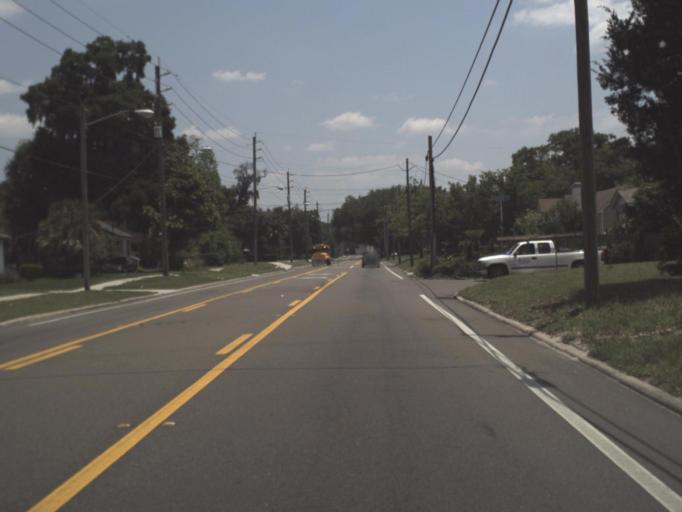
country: US
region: Florida
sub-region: Duval County
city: Jacksonville
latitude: 30.3838
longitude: -81.6543
